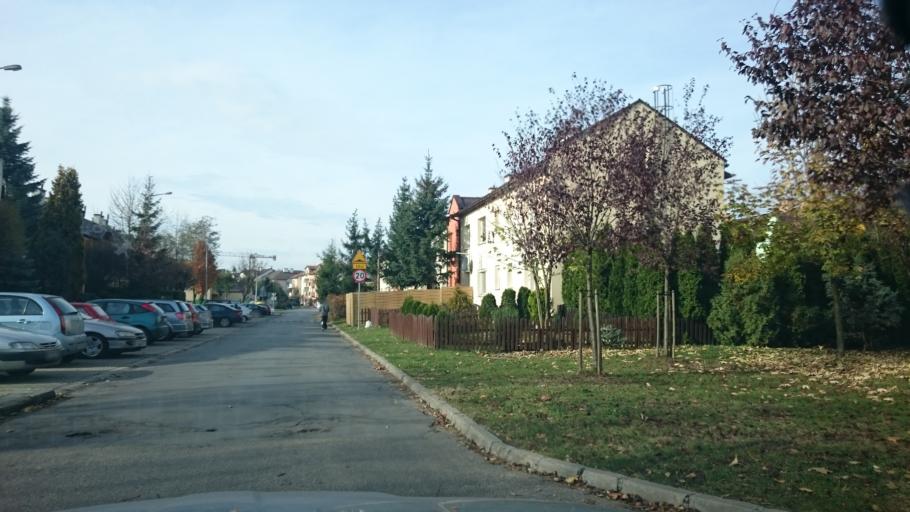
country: PL
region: Lesser Poland Voivodeship
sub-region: Powiat wielicki
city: Czarnochowice
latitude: 50.0202
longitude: 20.0517
